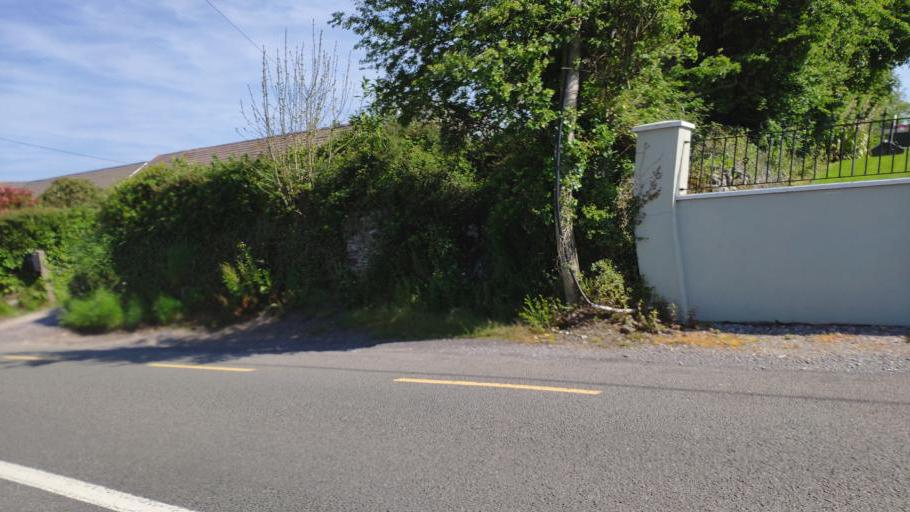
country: IE
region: Munster
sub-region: County Cork
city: Blarney
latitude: 51.9228
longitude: -8.5527
